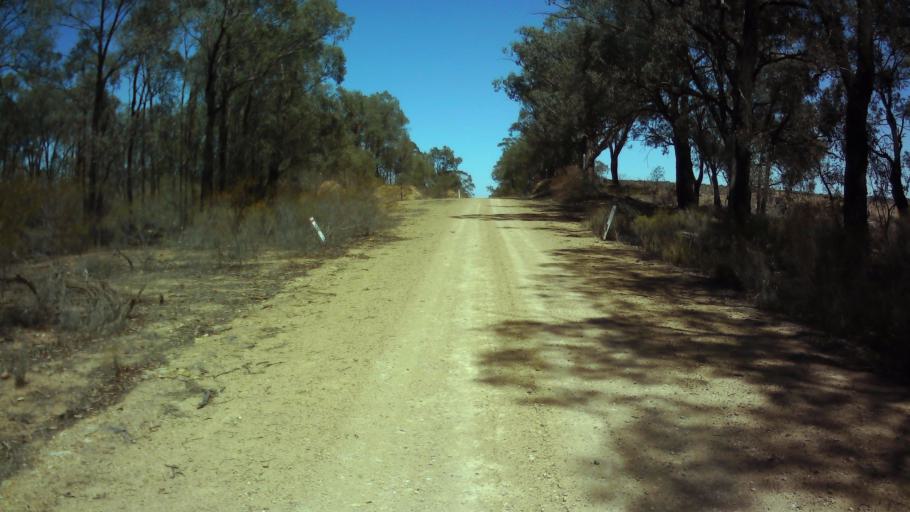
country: AU
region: New South Wales
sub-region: Forbes
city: Forbes
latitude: -33.6953
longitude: 147.8362
